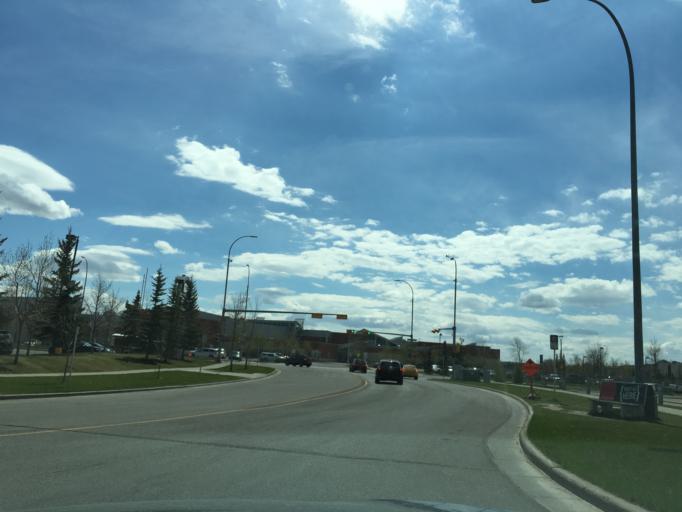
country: CA
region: Alberta
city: Calgary
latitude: 50.8996
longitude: -114.0664
